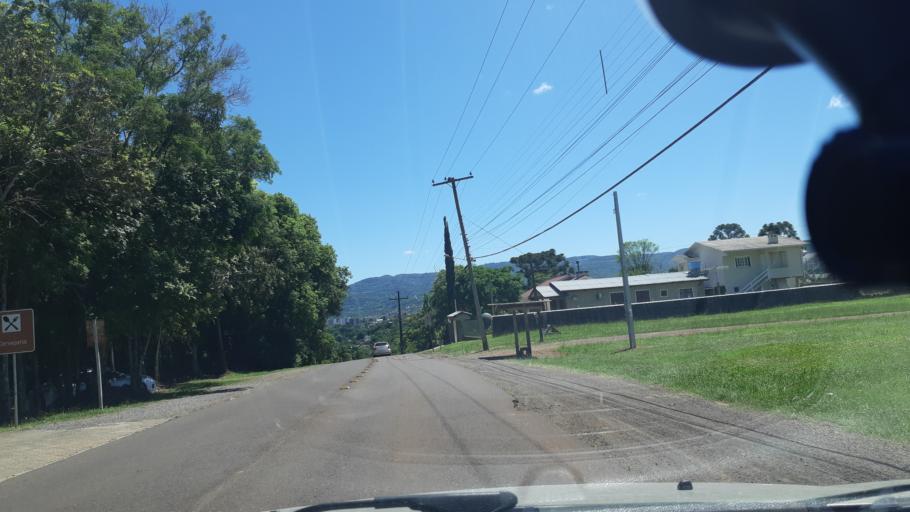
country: BR
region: Rio Grande do Sul
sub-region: Ivoti
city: Ivoti
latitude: -29.6113
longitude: -51.0916
